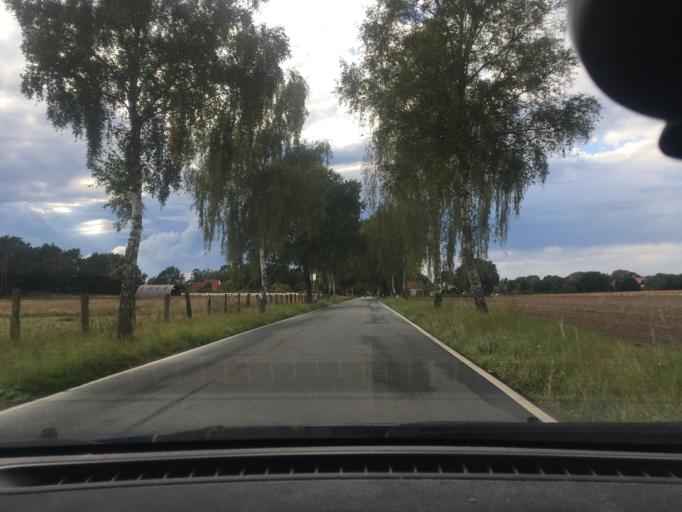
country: DE
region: Lower Saxony
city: Nahrendorf
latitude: 53.1710
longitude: 10.8232
